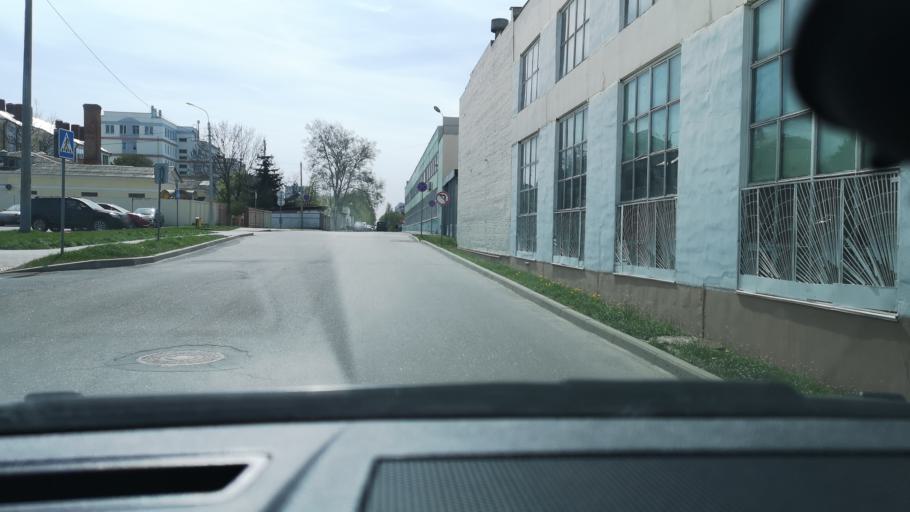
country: BY
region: Gomel
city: Gomel
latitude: 52.4216
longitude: 31.0098
